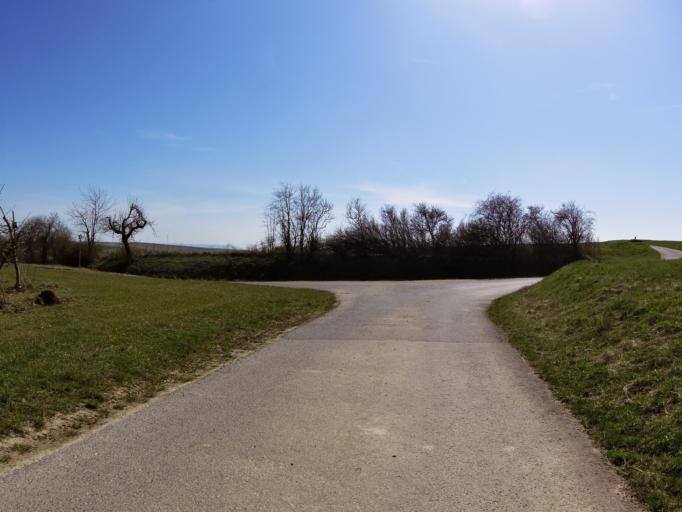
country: DE
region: Bavaria
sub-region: Regierungsbezirk Unterfranken
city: Prosselsheim
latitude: 49.8426
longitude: 10.1401
